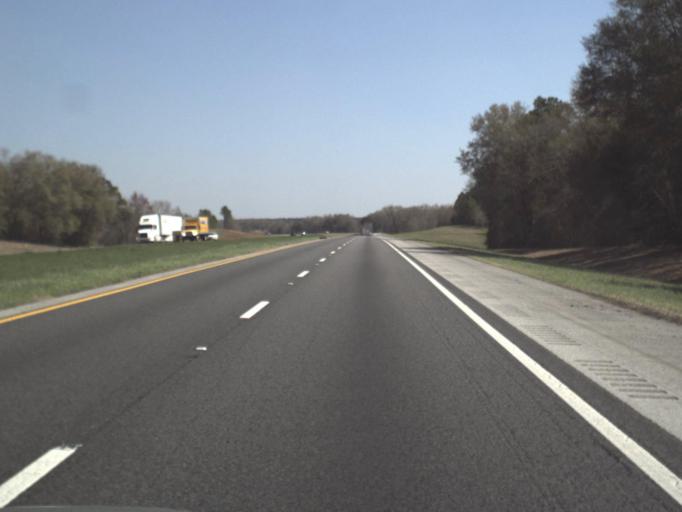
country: US
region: Florida
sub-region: Jackson County
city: Marianna
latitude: 30.6881
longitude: -85.1138
